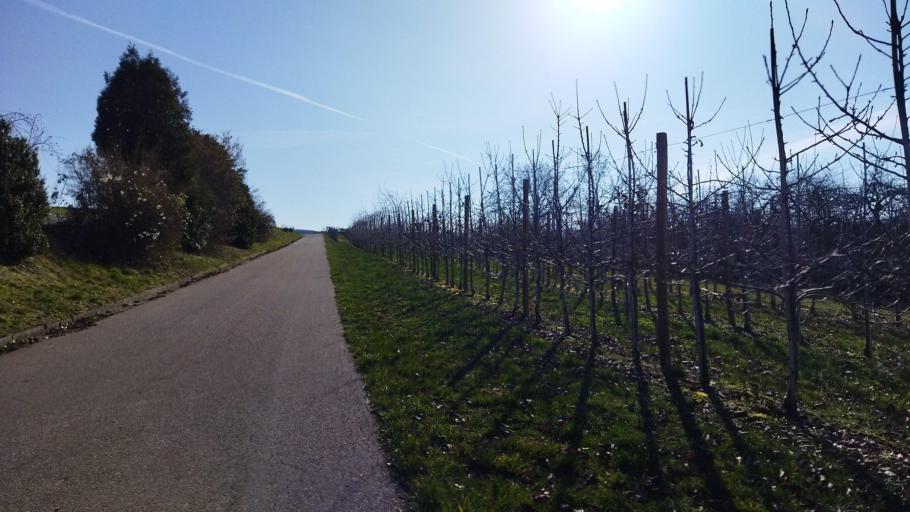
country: DE
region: Baden-Wuerttemberg
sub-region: Regierungsbezirk Stuttgart
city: Schwaigern
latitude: 49.1346
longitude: 9.0675
